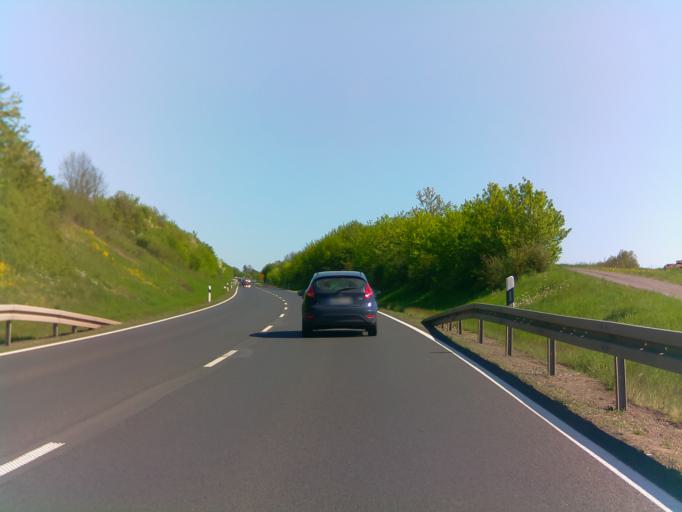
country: DE
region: Hesse
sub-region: Regierungsbezirk Giessen
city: Alsfeld
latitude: 50.7096
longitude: 9.3021
